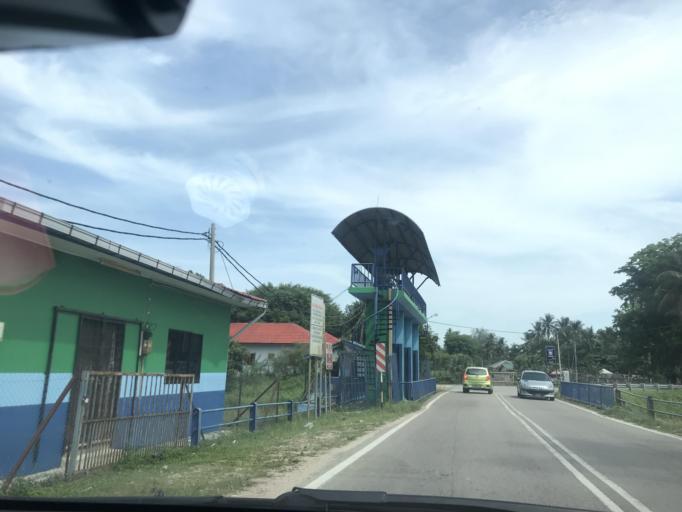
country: MY
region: Kelantan
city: Tumpat
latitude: 6.2064
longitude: 102.1441
